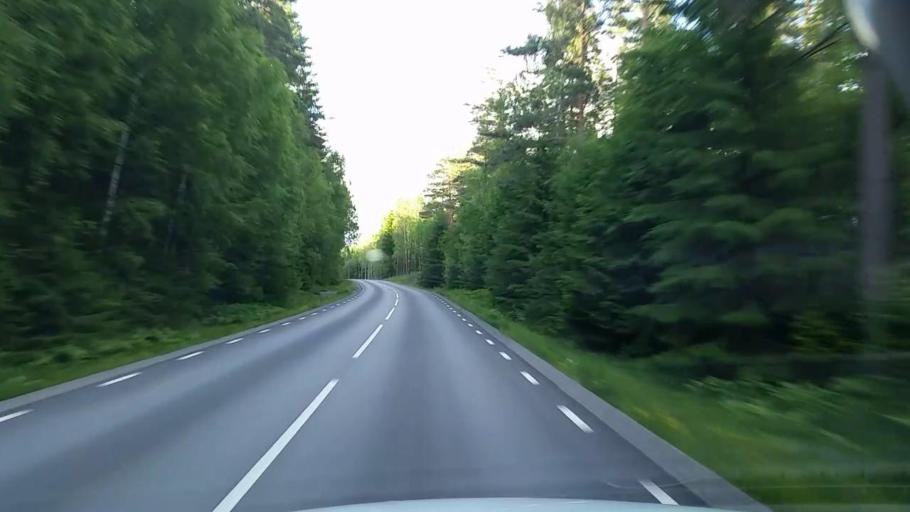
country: SE
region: Vaestmanland
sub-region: Kopings Kommun
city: Kolsva
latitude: 59.6466
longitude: 15.8317
